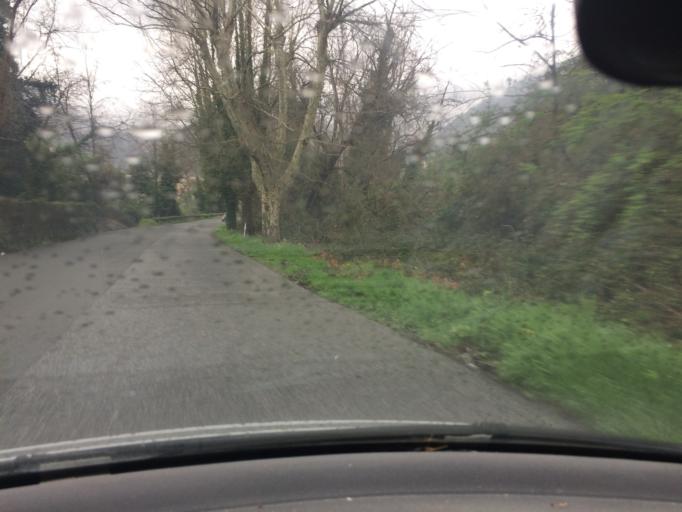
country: IT
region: Tuscany
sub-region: Provincia di Massa-Carrara
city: Carrara
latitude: 44.0722
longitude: 10.1059
